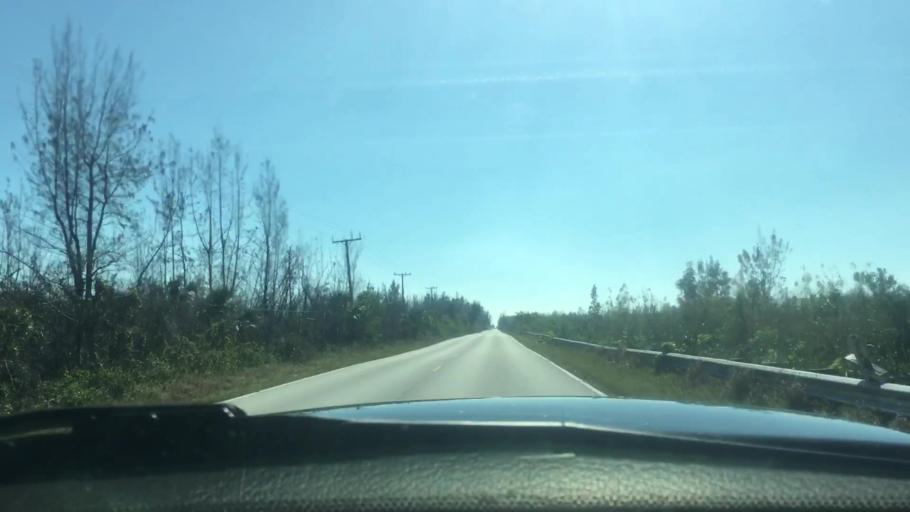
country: US
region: Florida
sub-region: Miami-Dade County
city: Florida City
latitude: 25.4253
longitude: -80.4678
